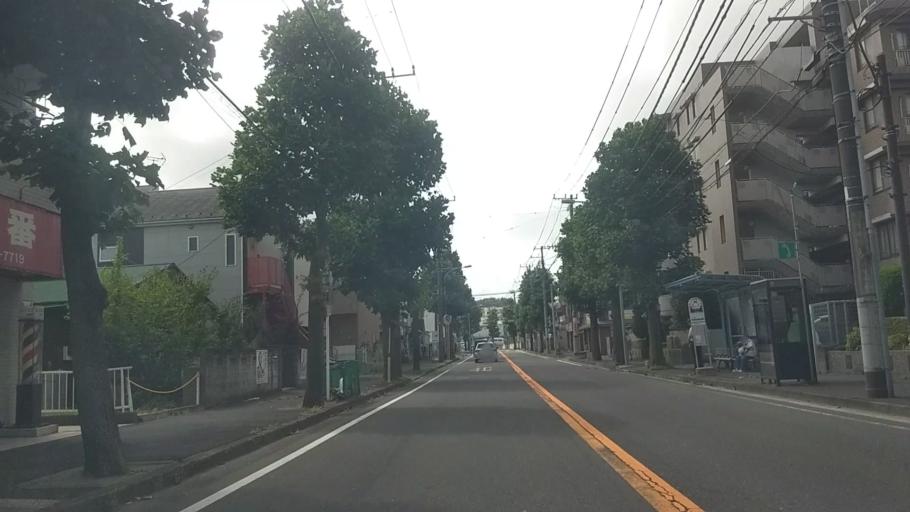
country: JP
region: Kanagawa
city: Yokohama
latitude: 35.3862
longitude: 139.6019
